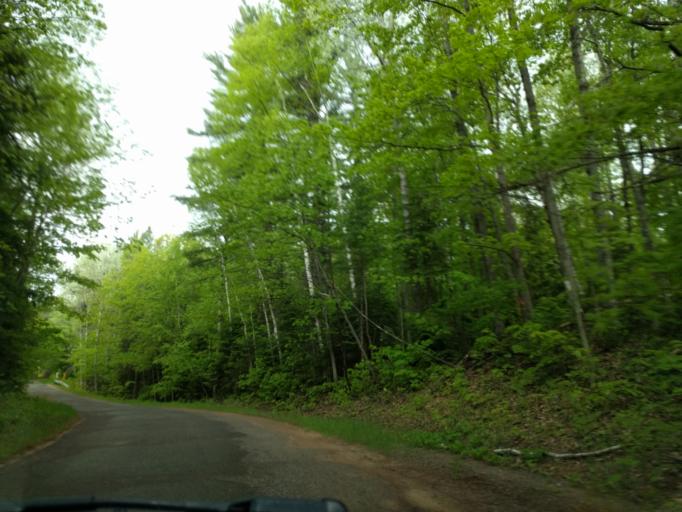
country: US
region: Michigan
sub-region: Marquette County
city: Trowbridge Park
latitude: 46.5747
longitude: -87.4768
